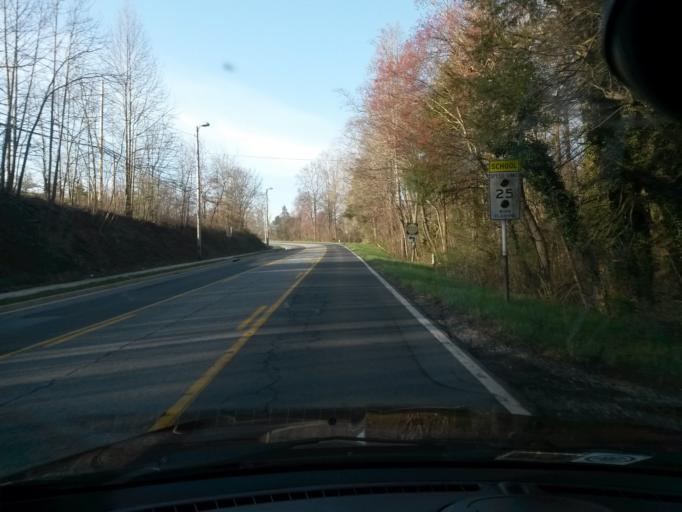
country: US
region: Virginia
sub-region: Amherst County
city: Amherst
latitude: 37.5715
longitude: -79.0599
